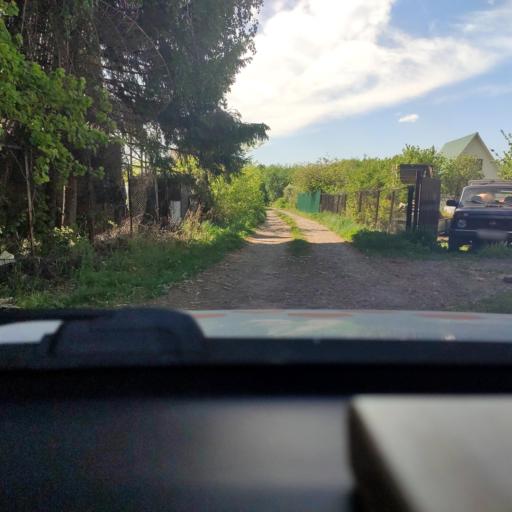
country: RU
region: Bashkortostan
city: Kabakovo
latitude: 54.6626
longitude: 56.1037
